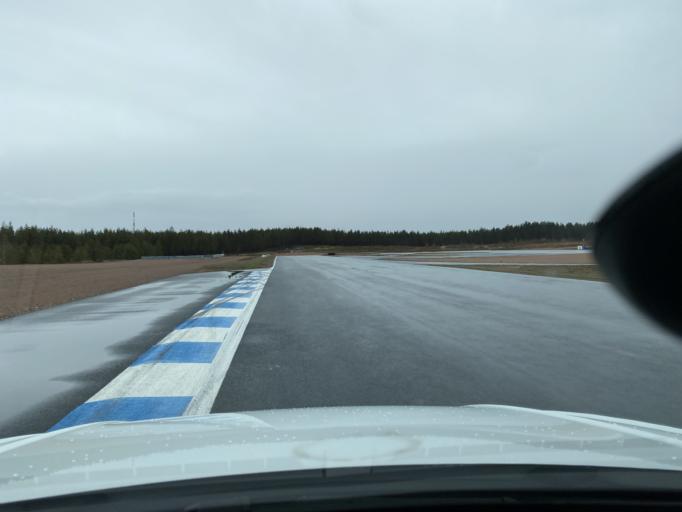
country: FI
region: Satakunta
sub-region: Pori
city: Vampula
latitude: 60.9779
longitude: 22.6678
